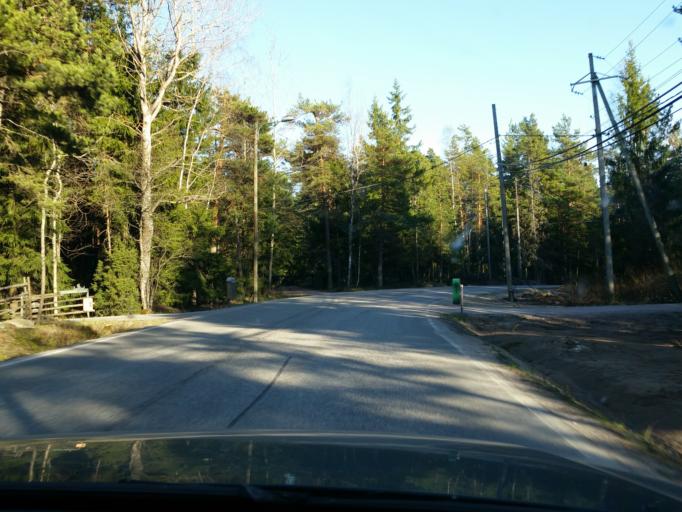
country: FI
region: Uusimaa
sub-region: Helsinki
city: Espoo
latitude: 60.1075
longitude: 24.5673
